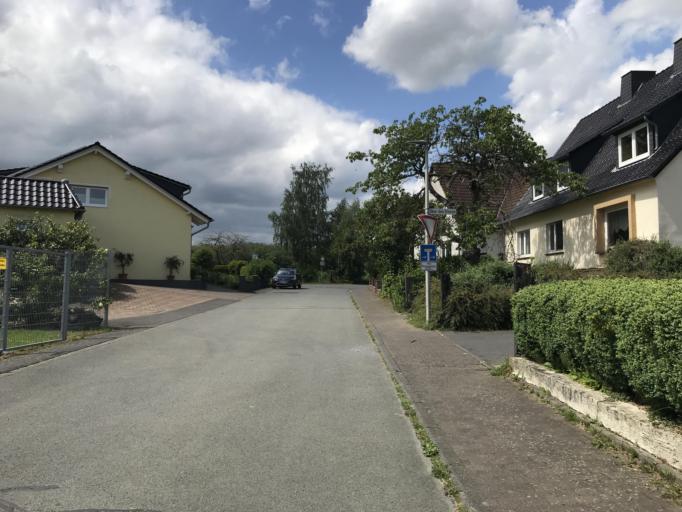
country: DE
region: Hesse
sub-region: Regierungsbezirk Kassel
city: Baunatal
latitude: 51.2747
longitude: 9.3674
